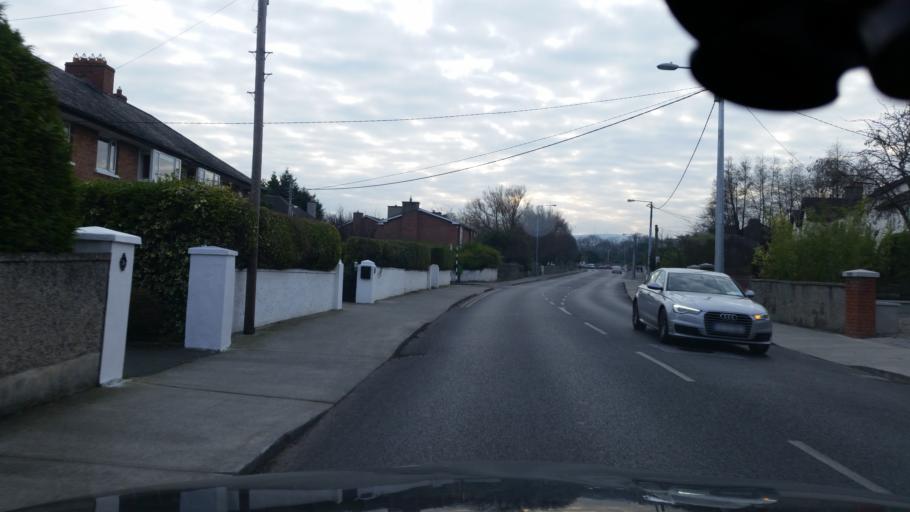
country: IE
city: Booterstown
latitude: 53.3032
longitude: -6.1993
